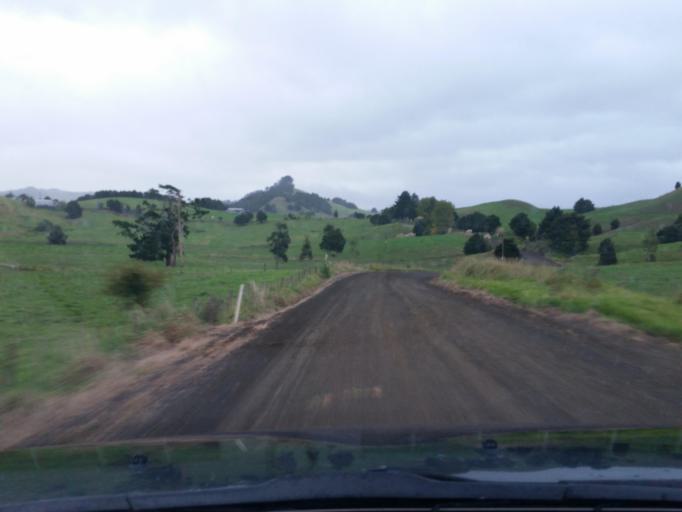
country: NZ
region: Northland
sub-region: Kaipara District
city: Dargaville
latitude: -35.8788
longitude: 174.0064
